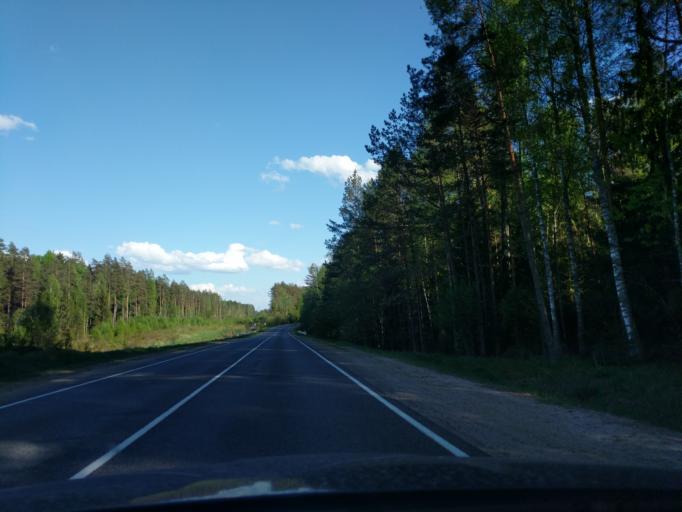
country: BY
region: Minsk
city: Myadzyel
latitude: 54.7879
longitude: 27.0312
